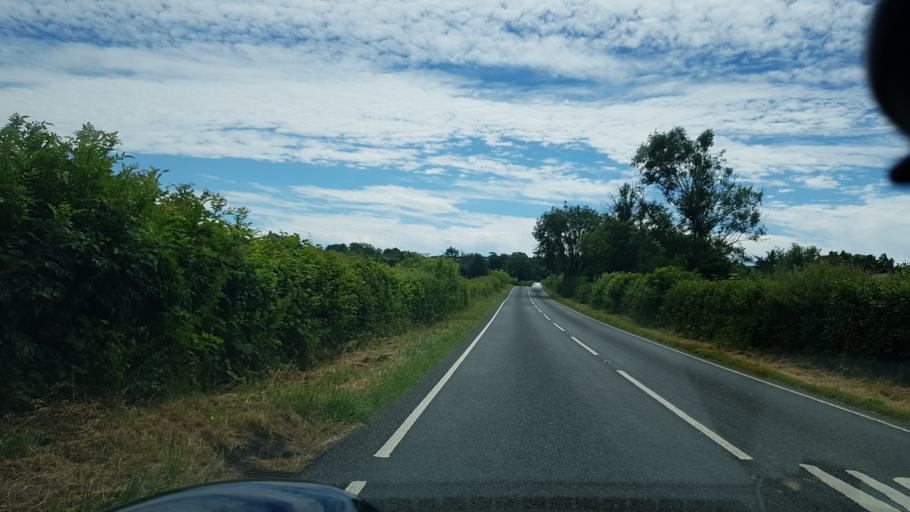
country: GB
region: Wales
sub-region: Carmarthenshire
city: Saint Clears
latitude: 51.7922
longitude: -4.4842
